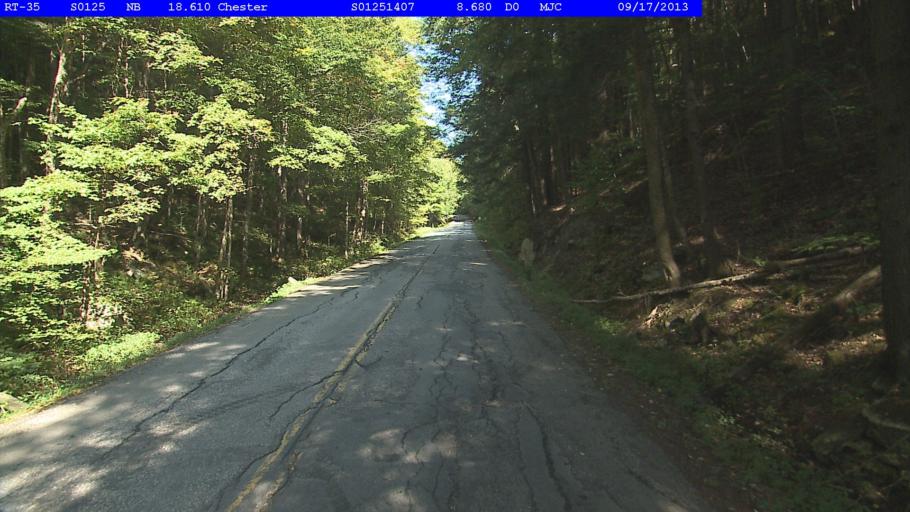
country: US
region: Vermont
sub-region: Windsor County
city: Chester
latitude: 43.2307
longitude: -72.6064
